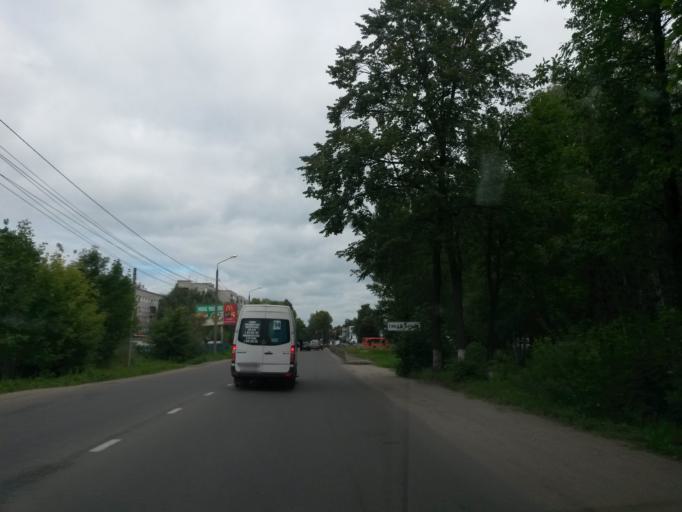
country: RU
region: Jaroslavl
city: Yaroslavl
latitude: 57.5911
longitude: 39.8775
